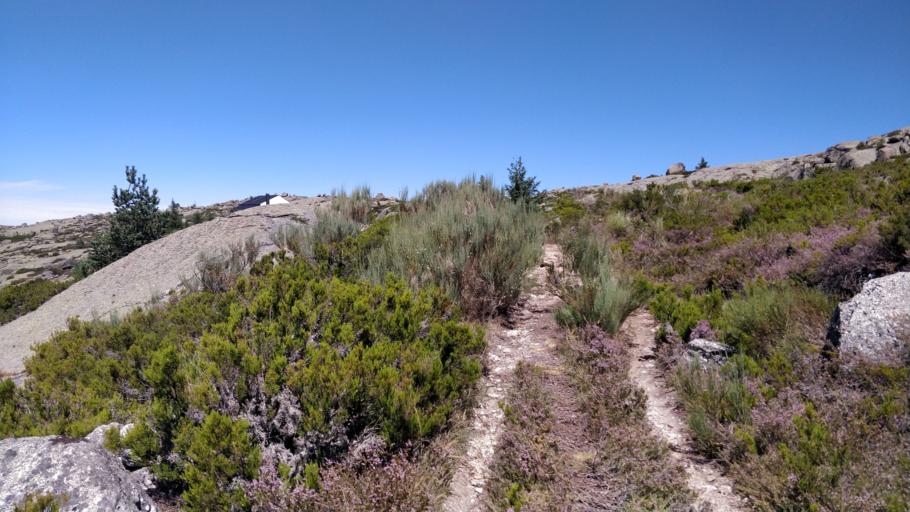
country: PT
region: Guarda
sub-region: Manteigas
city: Manteigas
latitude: 40.3614
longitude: -7.6272
